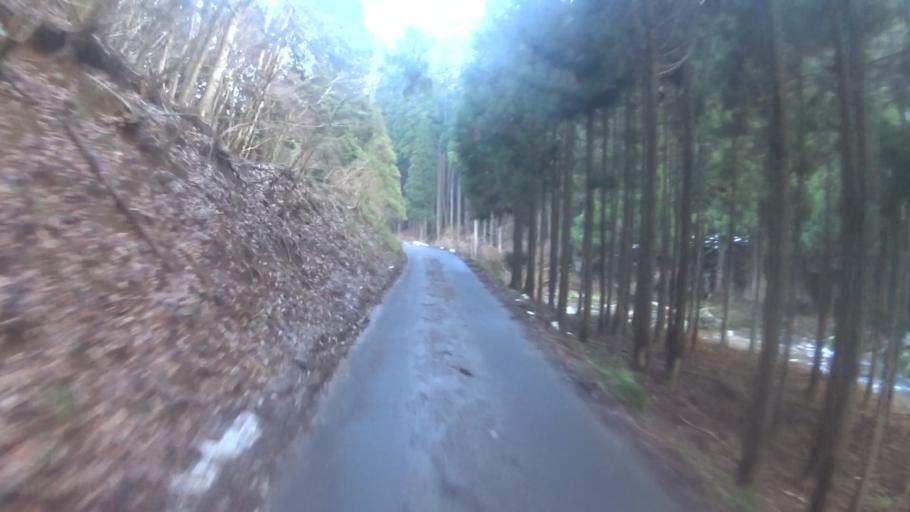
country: JP
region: Kyoto
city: Maizuru
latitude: 35.3961
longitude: 135.4910
